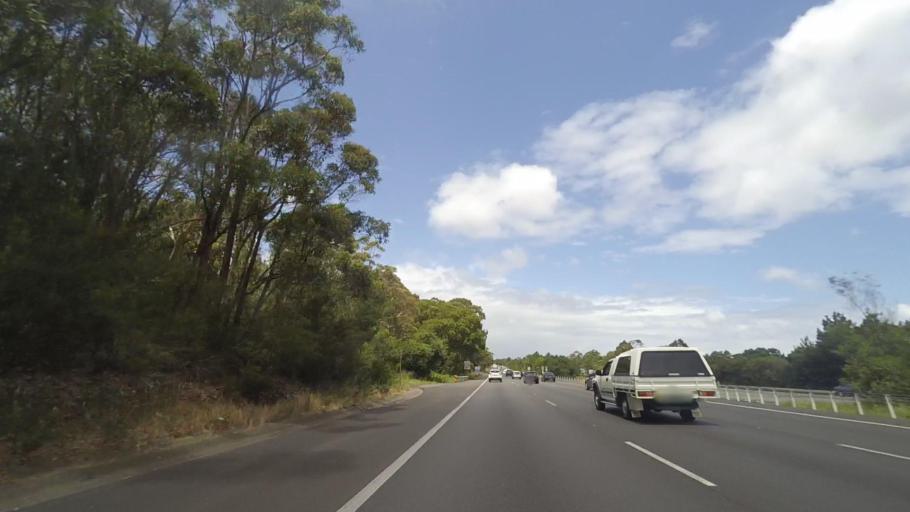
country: AU
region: New South Wales
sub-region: Gosford Shire
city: Narara
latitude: -33.3669
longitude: 151.3200
